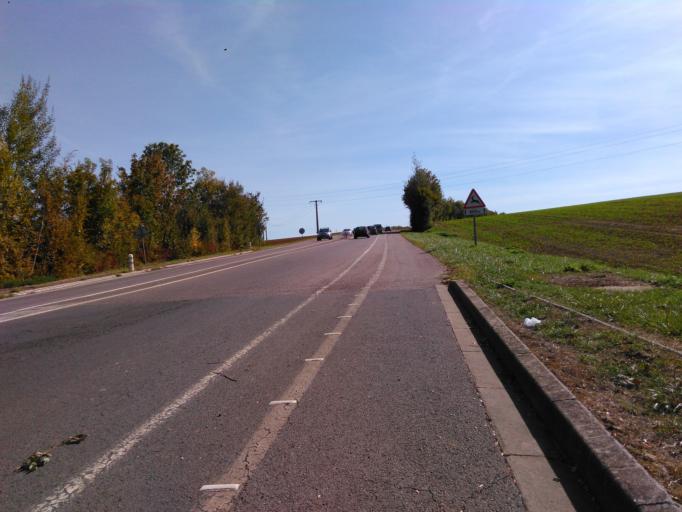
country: FR
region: Lorraine
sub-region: Departement de la Moselle
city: Hettange-Grande
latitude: 49.3929
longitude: 6.1668
